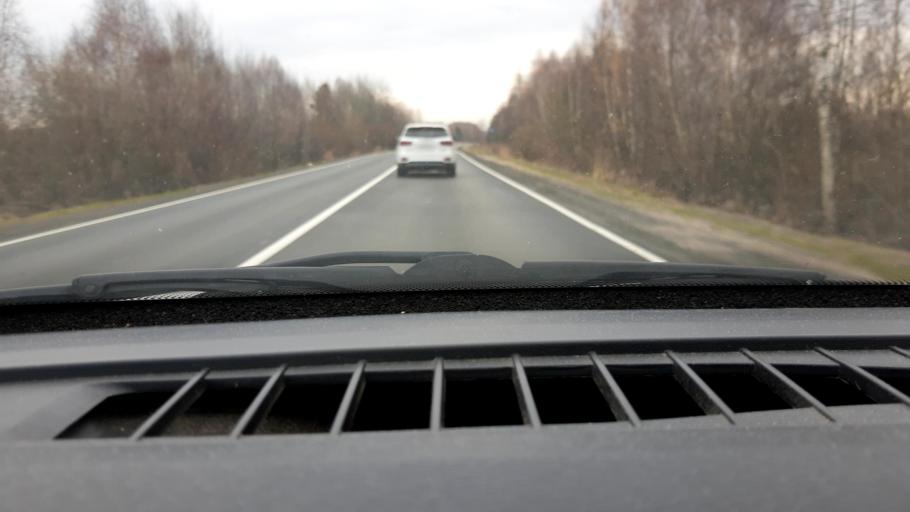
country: RU
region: Nizjnij Novgorod
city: Novaya Balakhna
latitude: 56.5750
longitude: 43.7015
